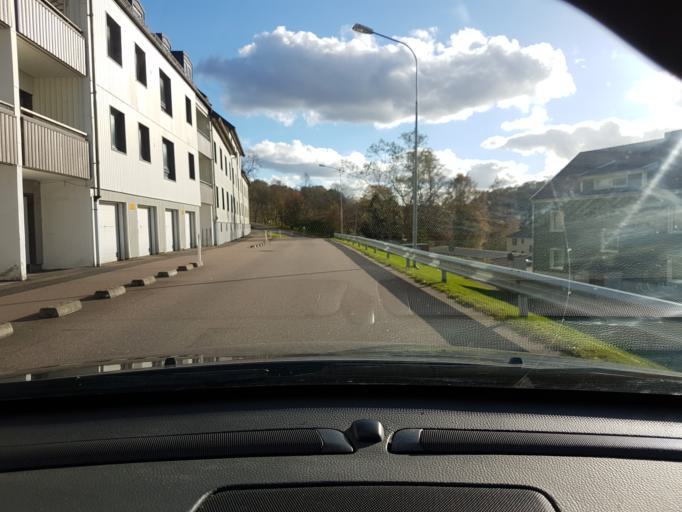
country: SE
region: Vaestra Goetaland
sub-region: Ale Kommun
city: Surte
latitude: 57.8314
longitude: 12.0214
